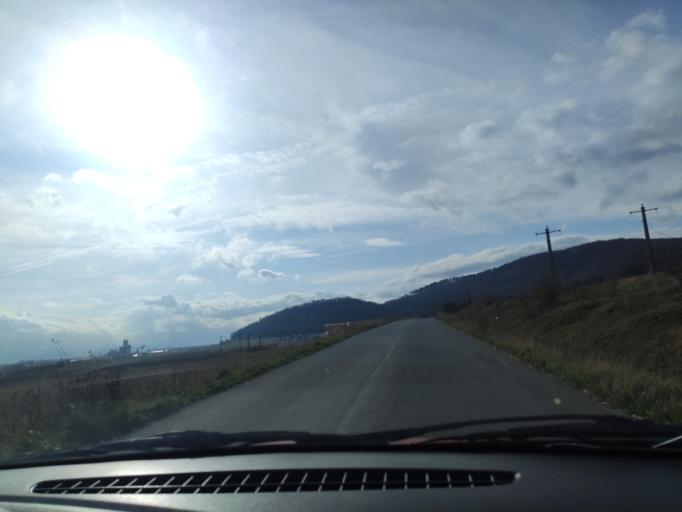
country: RO
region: Brasov
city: Codlea
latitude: 45.7274
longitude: 25.4568
